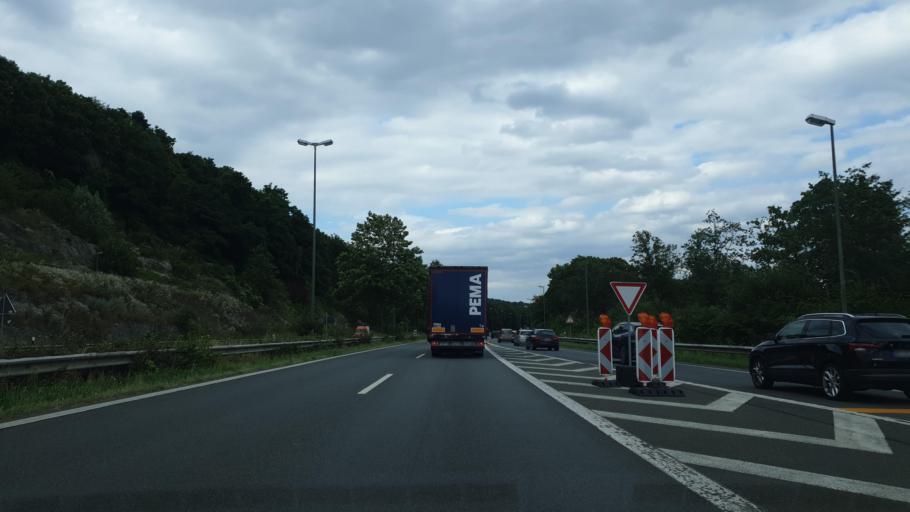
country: DE
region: North Rhine-Westphalia
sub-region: Regierungsbezirk Detmold
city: Bielefeld
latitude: 52.0039
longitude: 8.5022
